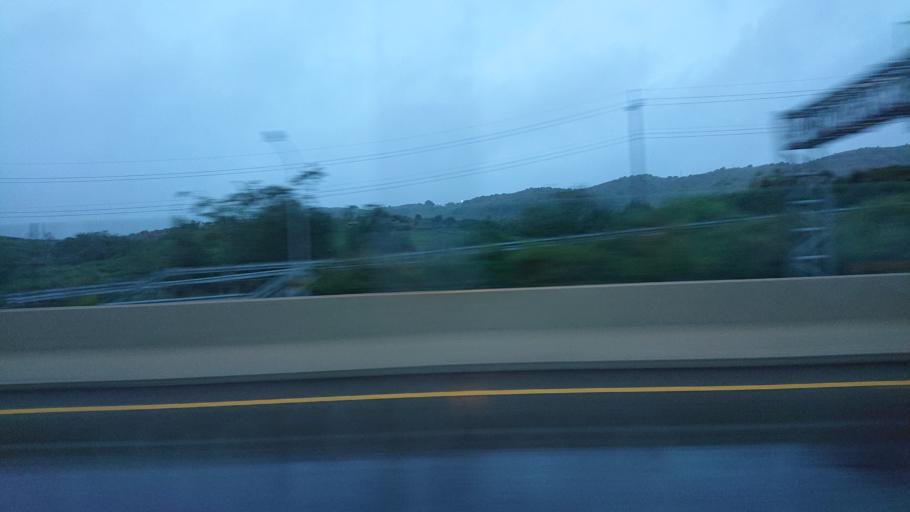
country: TW
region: Taiwan
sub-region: Miaoli
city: Miaoli
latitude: 24.5454
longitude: 120.7027
